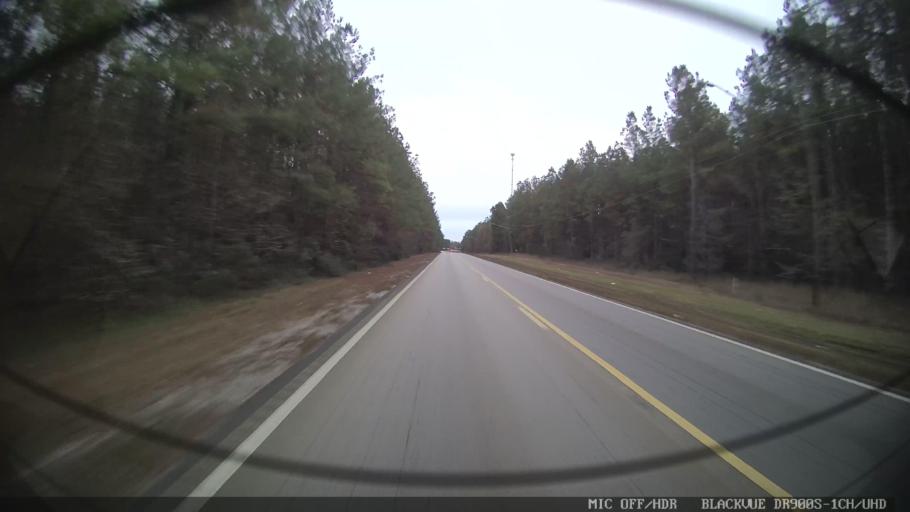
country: US
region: Mississippi
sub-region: Clarke County
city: Stonewall
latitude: 32.0527
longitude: -88.8973
